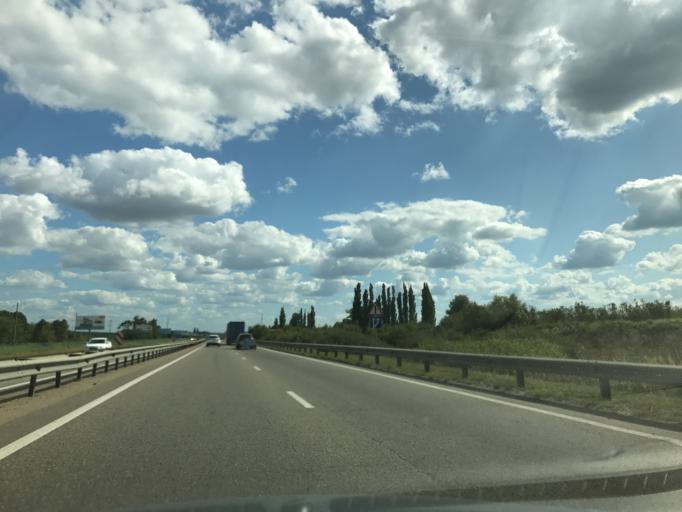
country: RU
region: Adygeya
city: Tlyustenkhabl'
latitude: 44.9305
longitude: 39.1378
